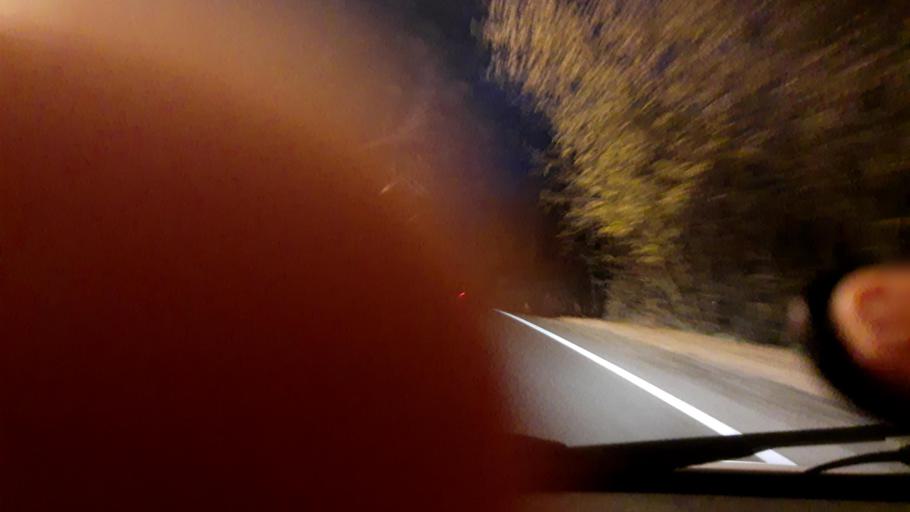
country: RU
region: Bashkortostan
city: Ufa
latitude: 54.8569
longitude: 56.0743
